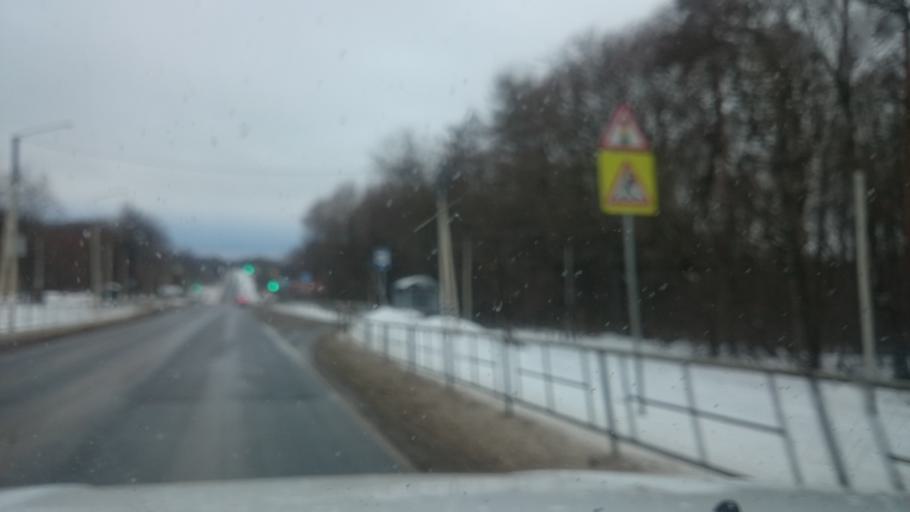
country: RU
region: Tula
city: Kosaya Gora
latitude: 54.0827
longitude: 37.5442
